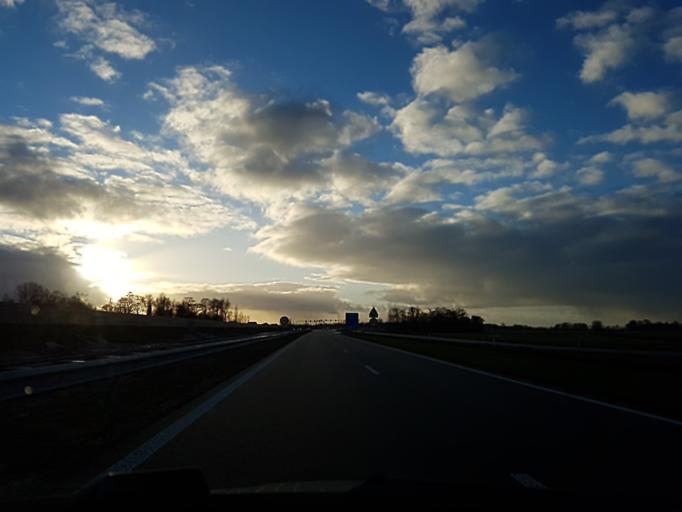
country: NL
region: Friesland
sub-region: Gemeente Tytsjerksteradiel
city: Hurdegaryp
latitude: 53.2202
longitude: 5.9350
